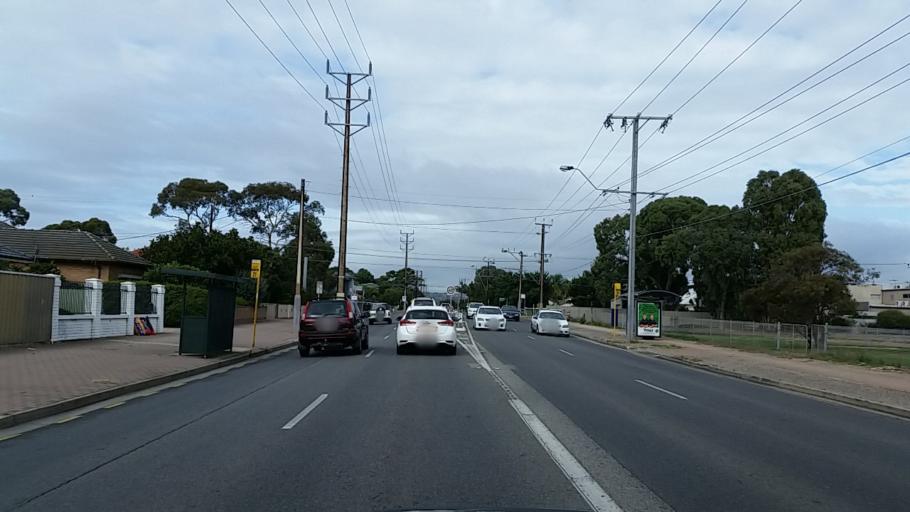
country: AU
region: South Australia
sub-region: Marion
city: Plympton Park
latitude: -34.9824
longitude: 138.5383
